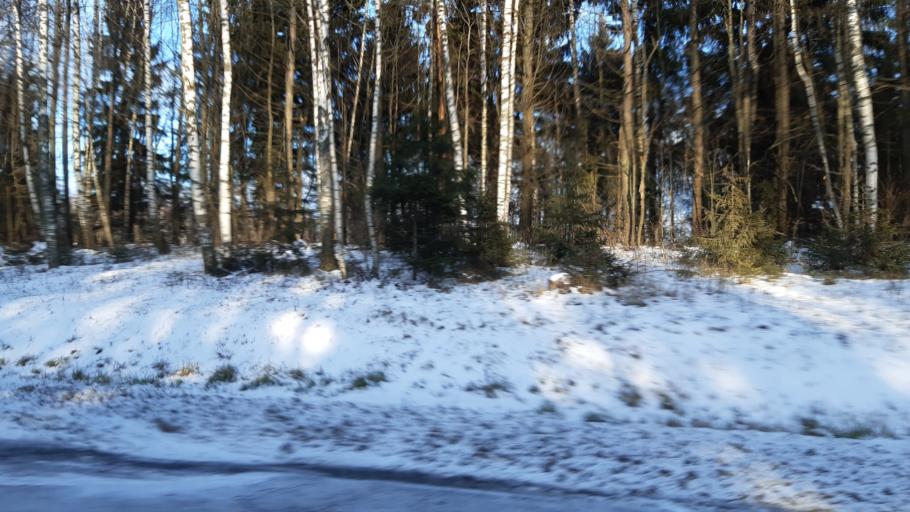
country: RU
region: Moskovskaya
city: Fryanovo
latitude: 56.2622
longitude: 38.4347
